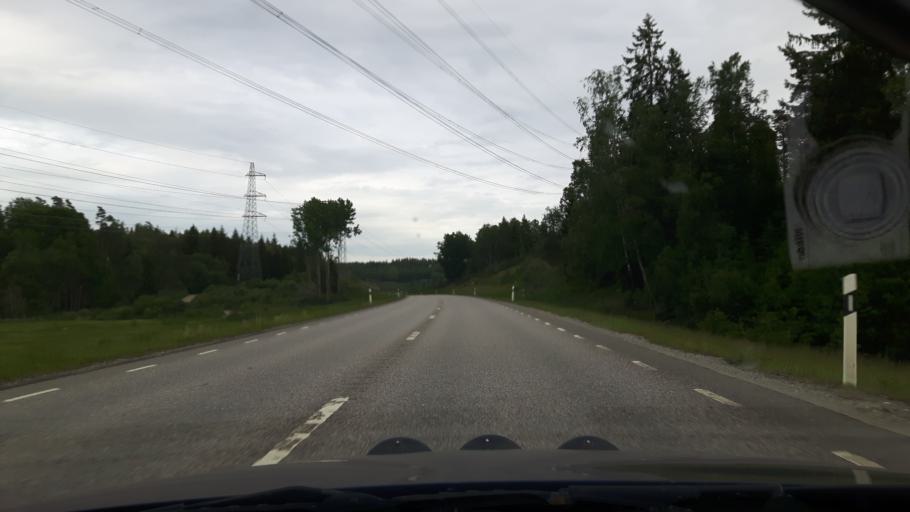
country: SE
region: Stockholm
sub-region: Sodertalje Kommun
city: Pershagen
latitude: 59.1751
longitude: 17.6914
